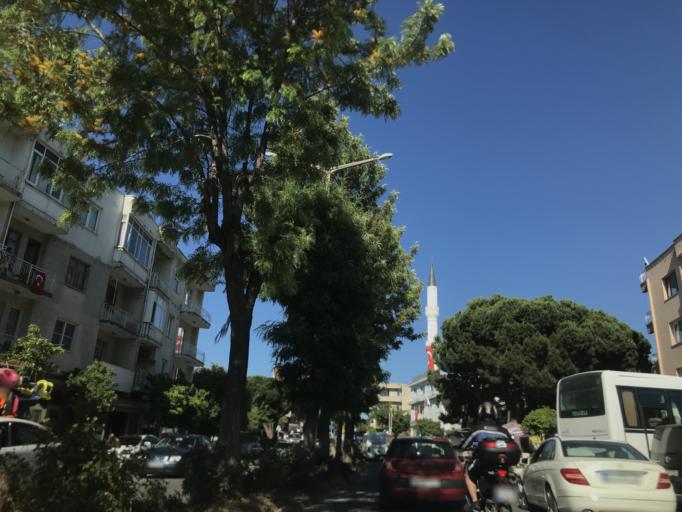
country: TR
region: Aydin
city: Davutlar
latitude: 37.7334
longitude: 27.2932
